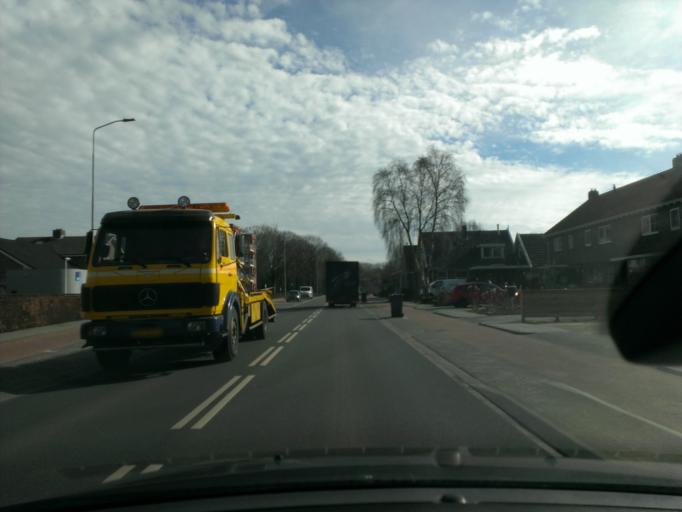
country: NL
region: Gelderland
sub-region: Gemeente Hattem
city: Hattem
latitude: 52.4595
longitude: 5.9970
